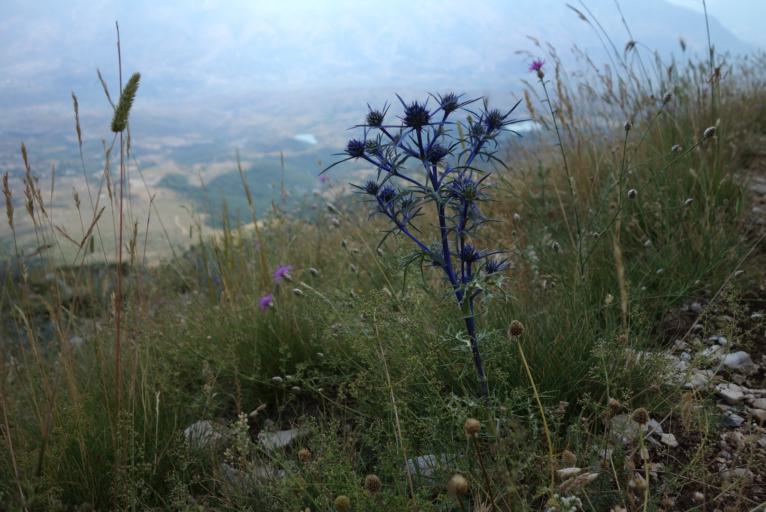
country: AL
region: Gjirokaster
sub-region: Rrethi i Gjirokastres
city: Saraqinishte
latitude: 40.1323
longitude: 20.2376
